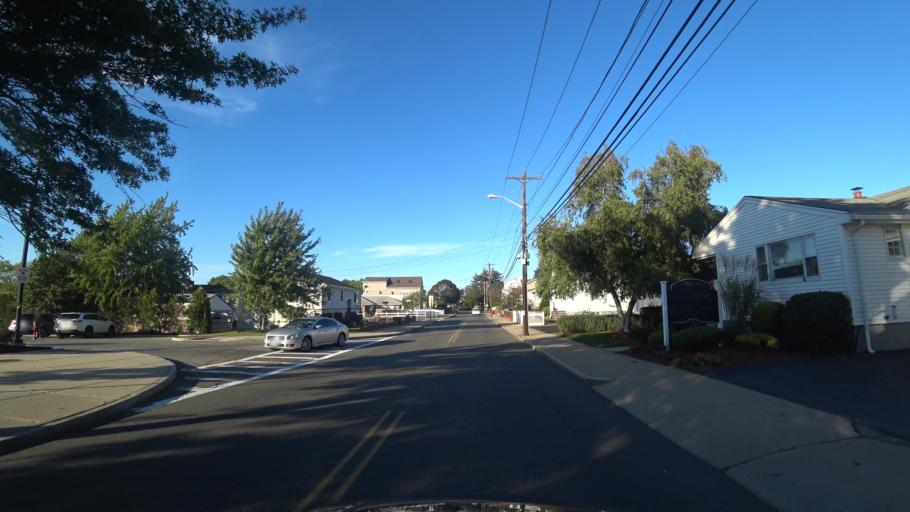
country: US
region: Massachusetts
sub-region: Suffolk County
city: Revere
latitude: 42.4198
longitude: -71.0181
